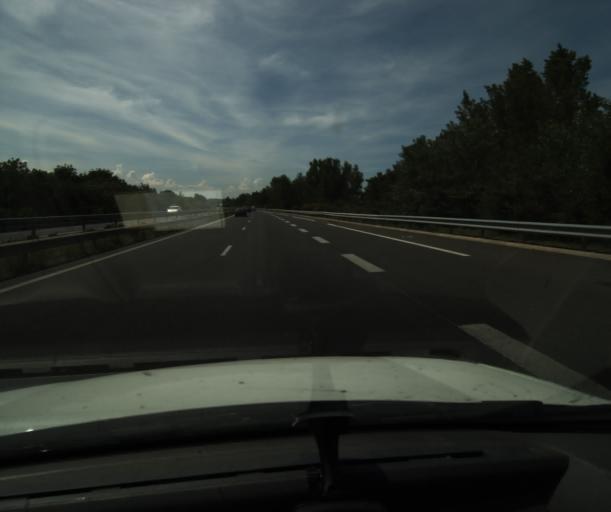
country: FR
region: Midi-Pyrenees
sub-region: Departement de la Haute-Garonne
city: Avignonet-Lauragais
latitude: 43.3554
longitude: 1.8028
